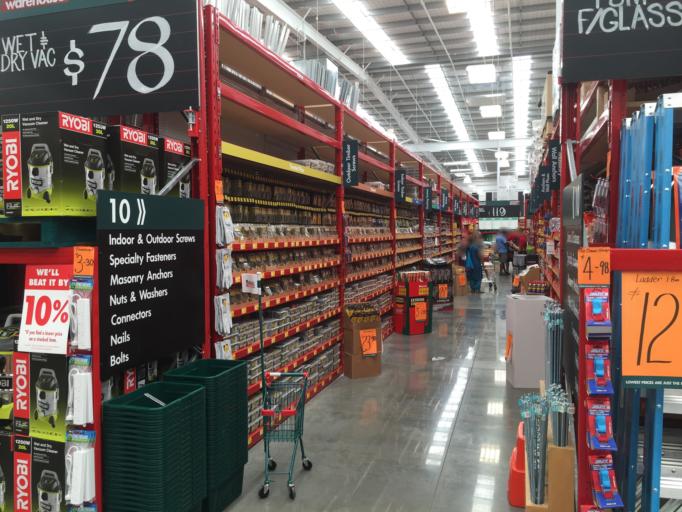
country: AU
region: New South Wales
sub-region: Blacktown
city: Hassall Grove
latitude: -33.7173
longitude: 150.8419
